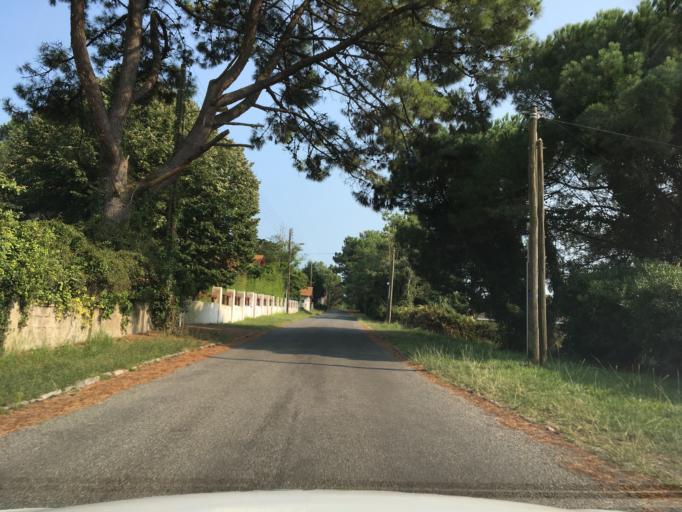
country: FR
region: Aquitaine
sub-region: Departement des Pyrenees-Atlantiques
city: Boucau
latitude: 43.5216
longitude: -1.5007
